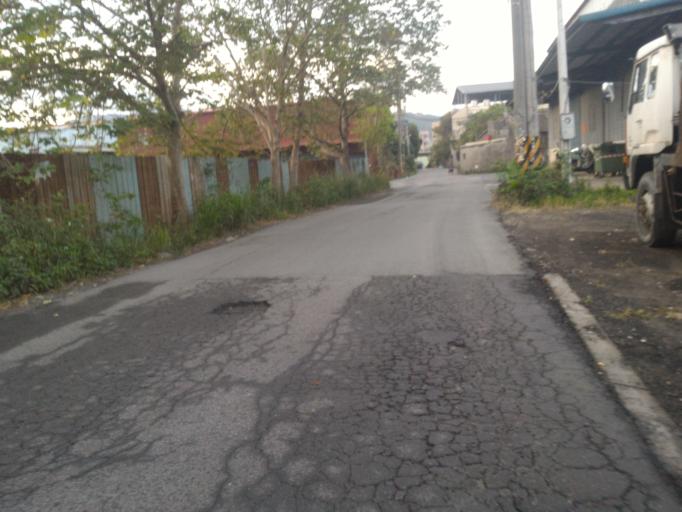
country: TW
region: Taiwan
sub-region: Taoyuan
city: Taoyuan
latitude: 24.9470
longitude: 121.3941
